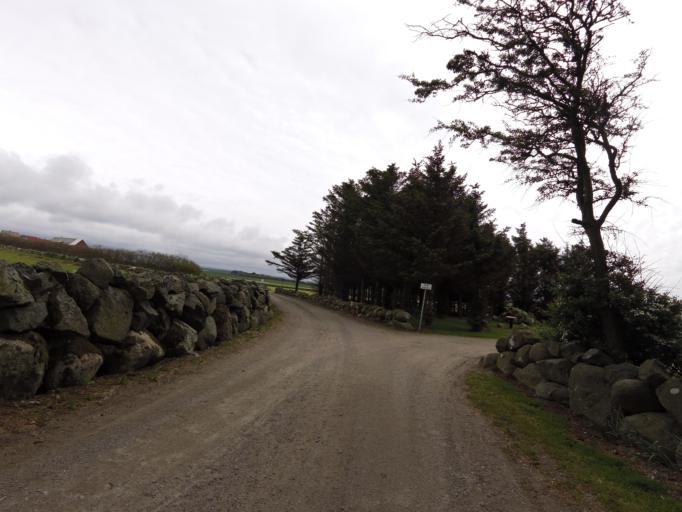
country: NO
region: Rogaland
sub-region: Ha
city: Naerbo
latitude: 58.6703
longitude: 5.5524
